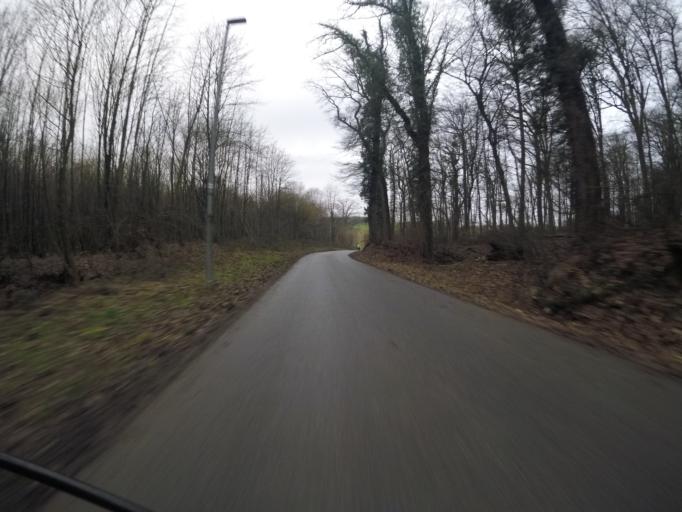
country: DE
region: Baden-Wuerttemberg
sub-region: Regierungsbezirk Stuttgart
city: Kirchberg an der Murr
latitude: 48.9450
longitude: 9.3594
